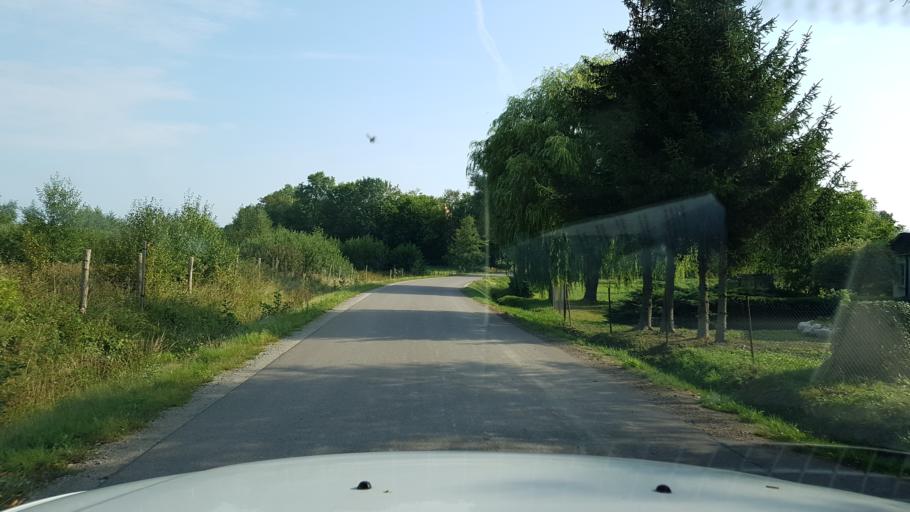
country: PL
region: West Pomeranian Voivodeship
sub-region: Powiat slawienski
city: Slawno
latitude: 54.3706
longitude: 16.5773
